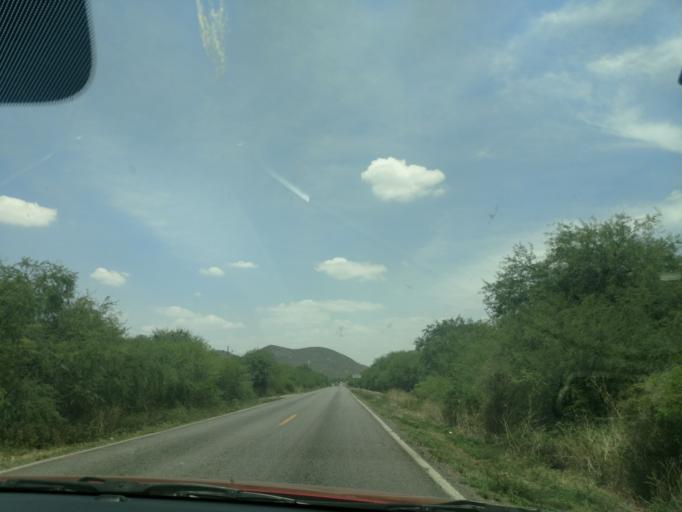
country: MX
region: San Luis Potosi
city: Ciudad Fernandez
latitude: 22.0086
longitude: -100.1531
